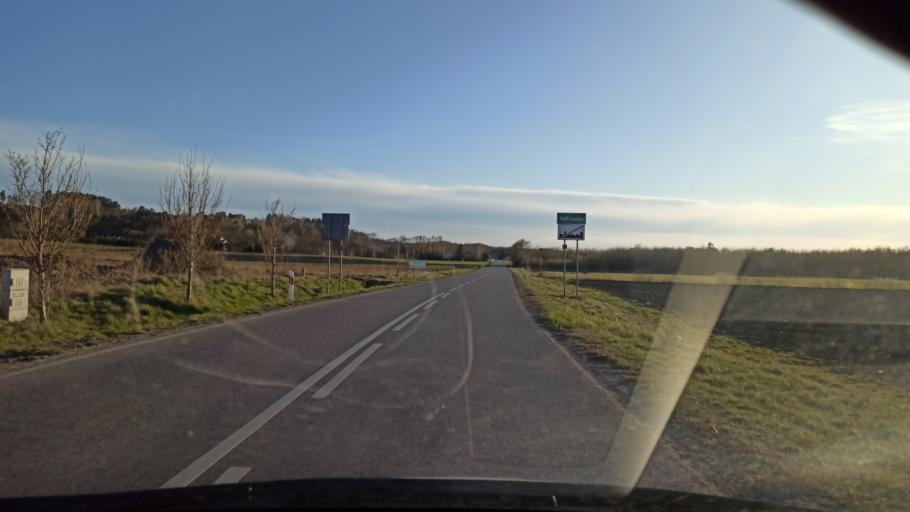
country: PL
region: Warmian-Masurian Voivodeship
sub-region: Powiat elblaski
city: Tolkmicko
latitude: 54.3104
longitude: 19.5186
